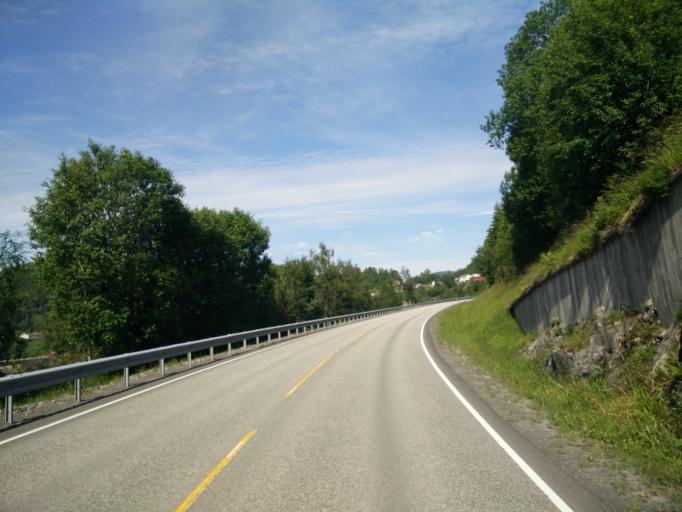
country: NO
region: More og Romsdal
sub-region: Kristiansund
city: Rensvik
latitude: 63.0161
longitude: 8.0034
